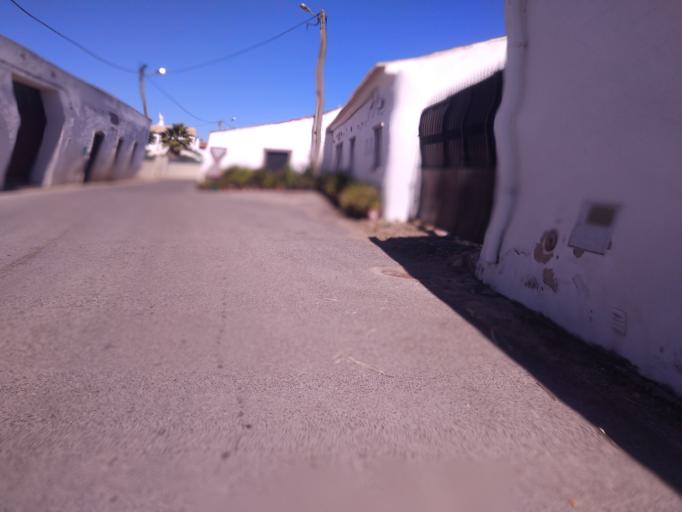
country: PT
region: Faro
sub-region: Sao Bras de Alportel
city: Sao Bras de Alportel
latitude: 37.1700
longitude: -7.8910
